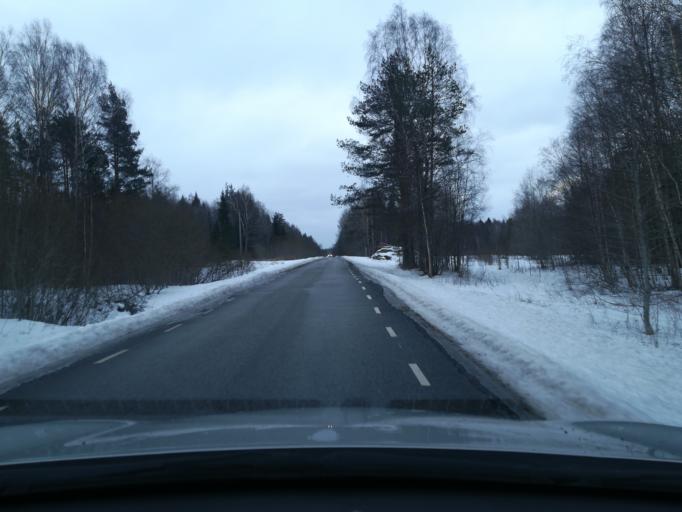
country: EE
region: Harju
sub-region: Nissi vald
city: Turba
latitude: 59.0659
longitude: 24.2527
